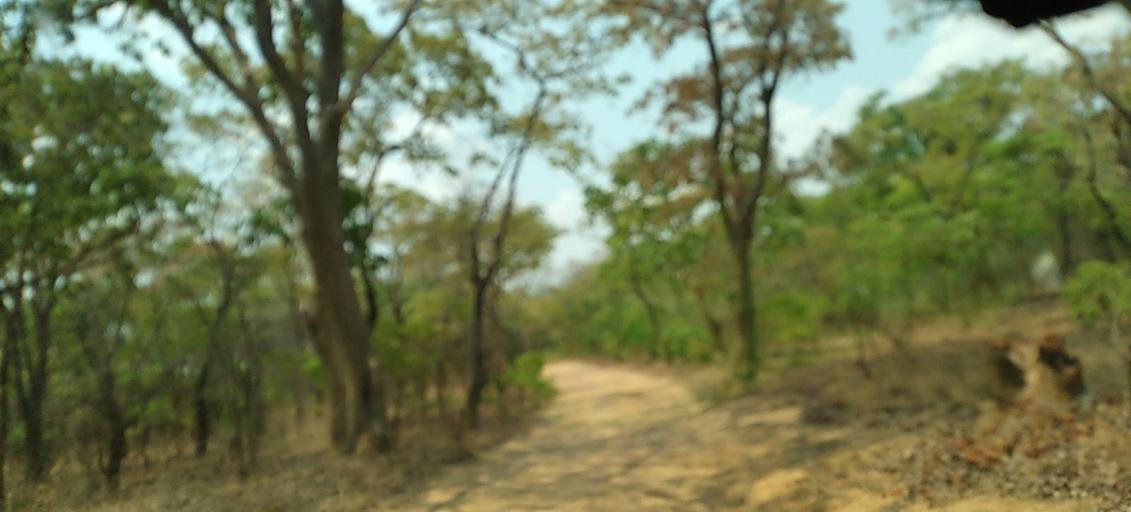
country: ZM
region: North-Western
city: Kabompo
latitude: -13.6496
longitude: 24.3753
